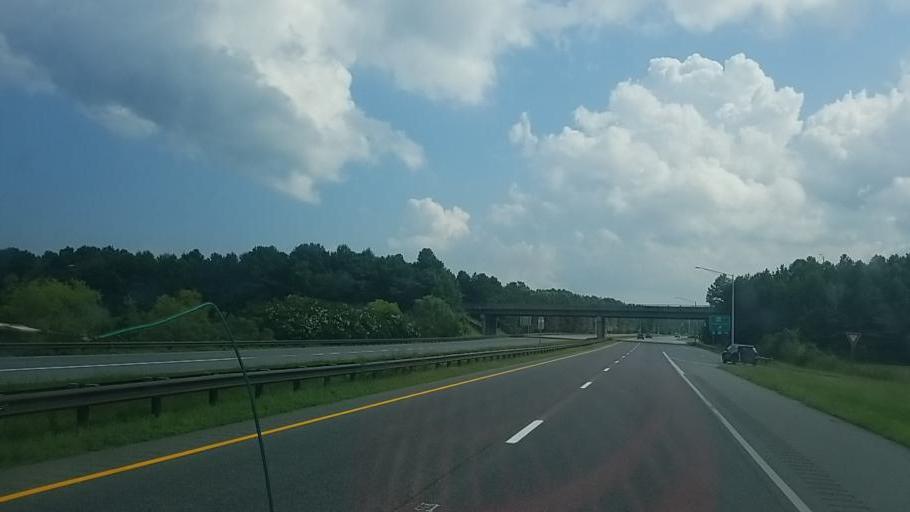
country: US
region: Maryland
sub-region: Worcester County
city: Ocean Pines
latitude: 38.3787
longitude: -75.2066
